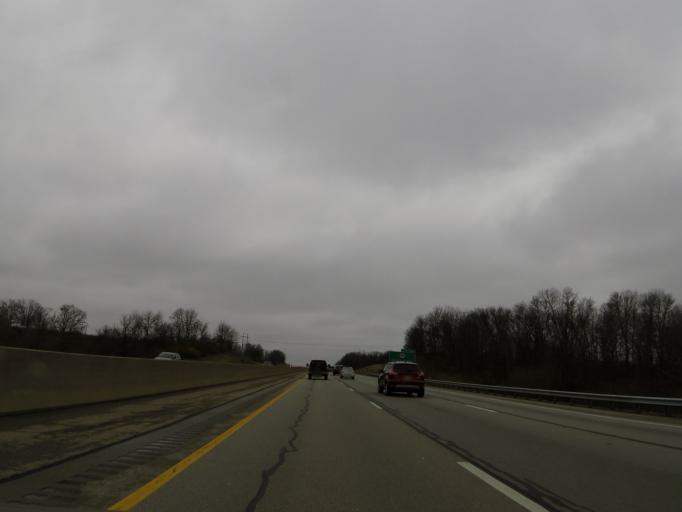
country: US
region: Kentucky
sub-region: Grant County
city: Crittenden
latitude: 38.8087
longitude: -84.6022
